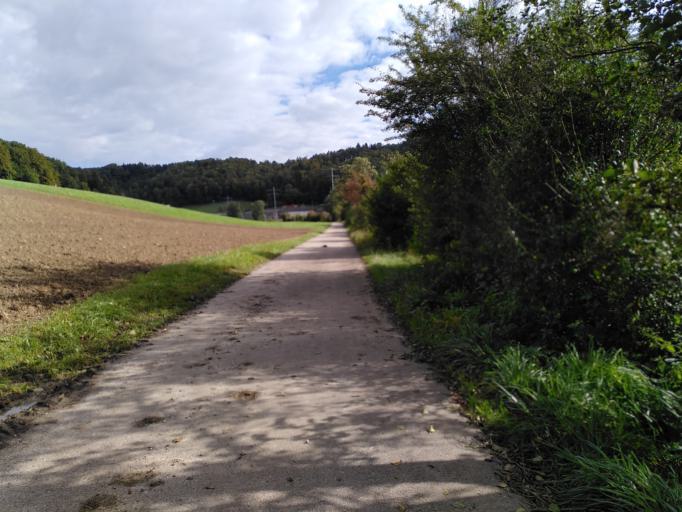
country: CH
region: Bern
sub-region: Oberaargau
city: Seeberg
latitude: 47.1392
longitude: 7.6897
